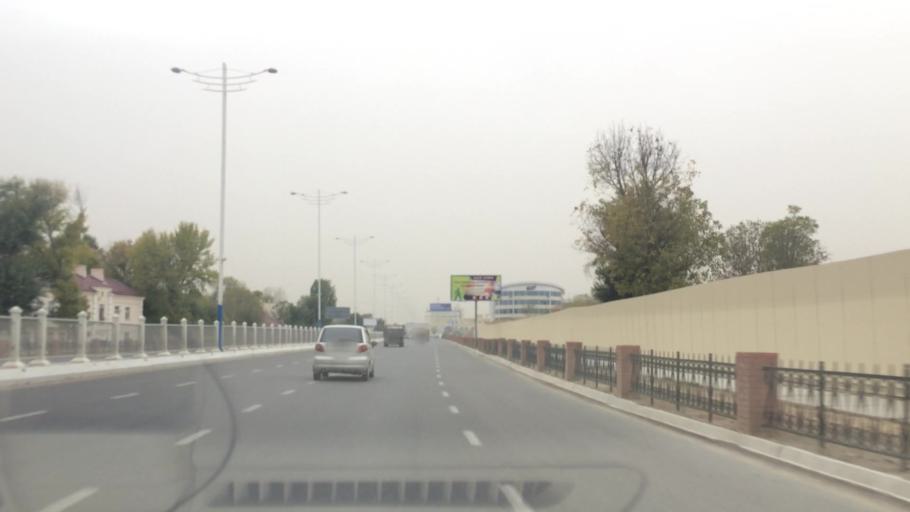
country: UZ
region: Toshkent
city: Salor
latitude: 41.3036
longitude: 69.3153
